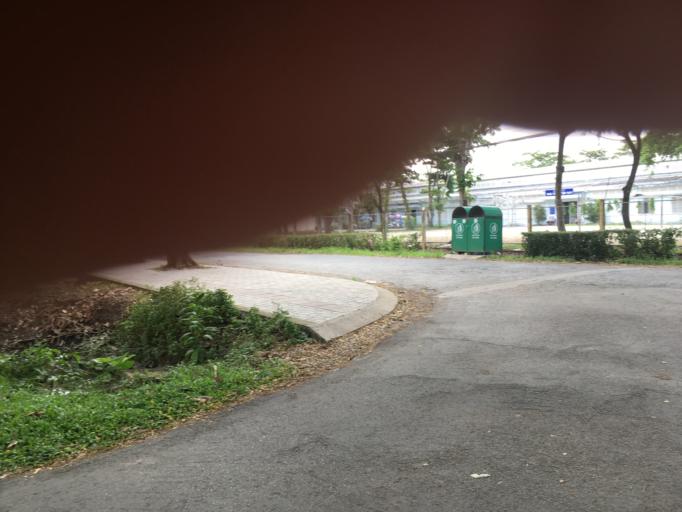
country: VN
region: Can Tho
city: Can Tho
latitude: 10.0323
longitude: 105.7691
